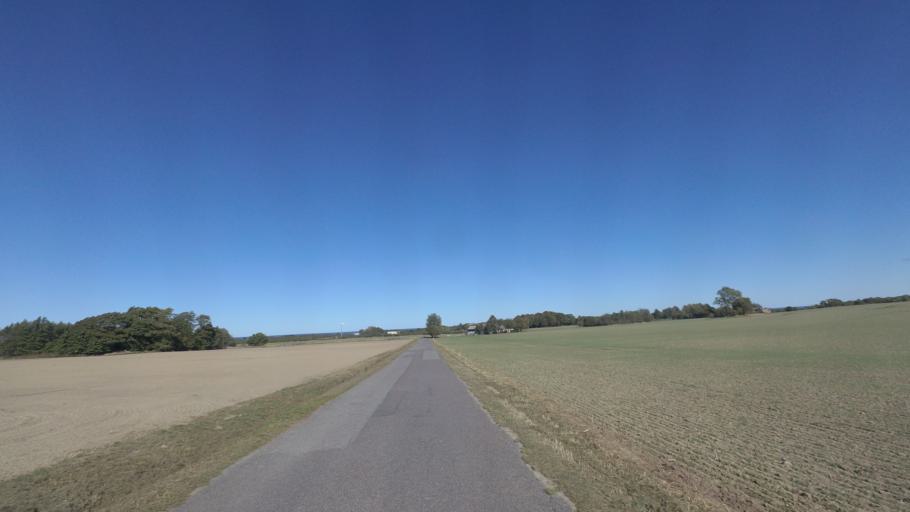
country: DK
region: Capital Region
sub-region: Bornholm Kommune
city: Nexo
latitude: 55.1187
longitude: 15.0464
